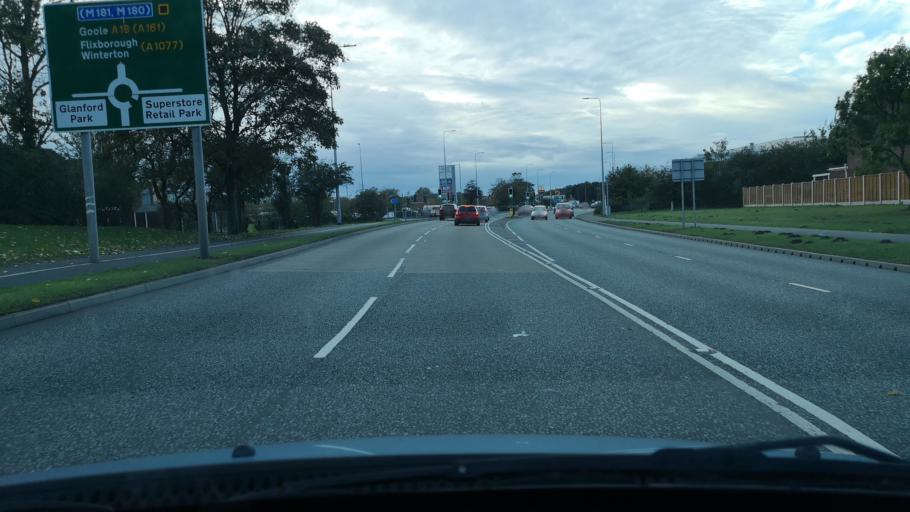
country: GB
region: England
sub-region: North Lincolnshire
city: Scunthorpe
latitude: 53.5891
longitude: -0.6902
